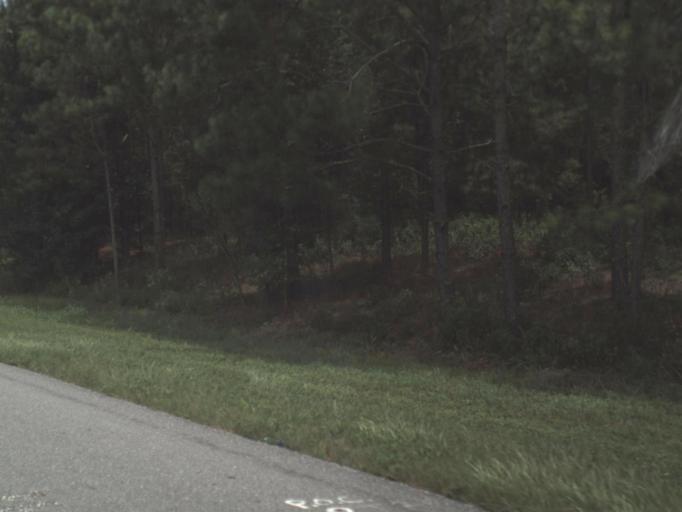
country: US
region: Florida
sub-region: Hernando County
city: Hill 'n Dale
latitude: 28.5004
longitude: -82.2474
